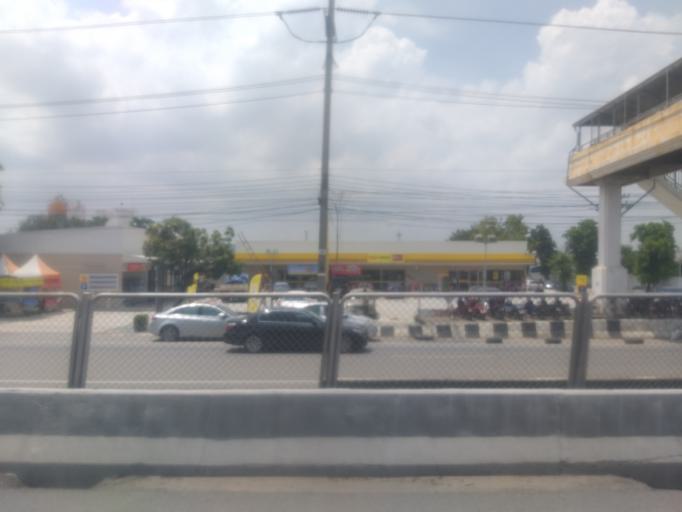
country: TH
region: Bangkok
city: Saphan Sung
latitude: 13.7340
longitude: 100.6915
